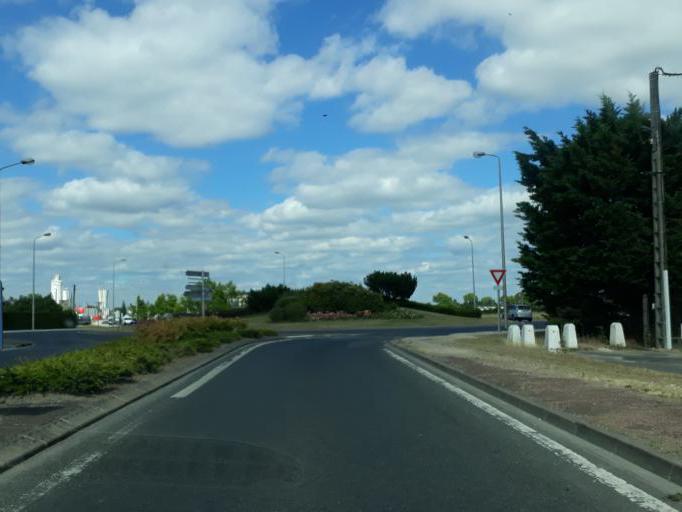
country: FR
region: Centre
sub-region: Departement du Loiret
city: Saint-Denis-en-Val
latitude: 47.8710
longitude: 1.9383
